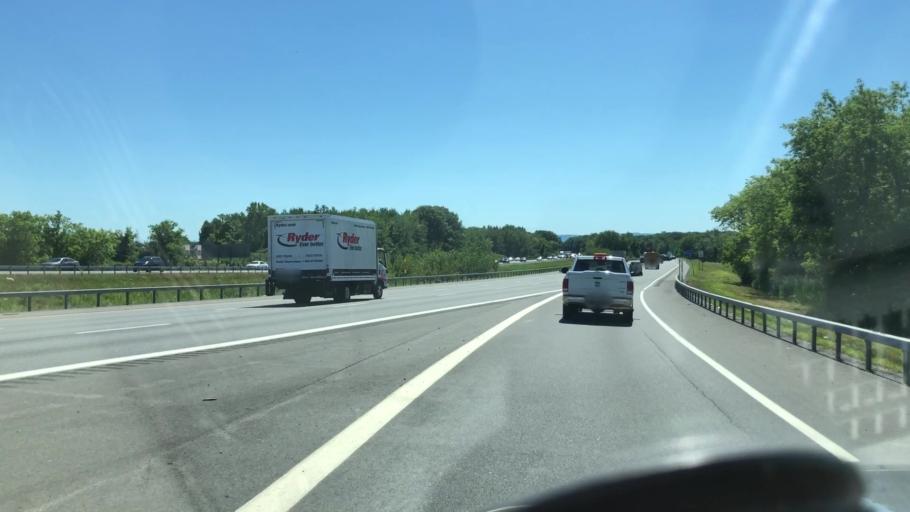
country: US
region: New York
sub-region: Albany County
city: Roessleville
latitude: 42.7274
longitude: -73.7989
